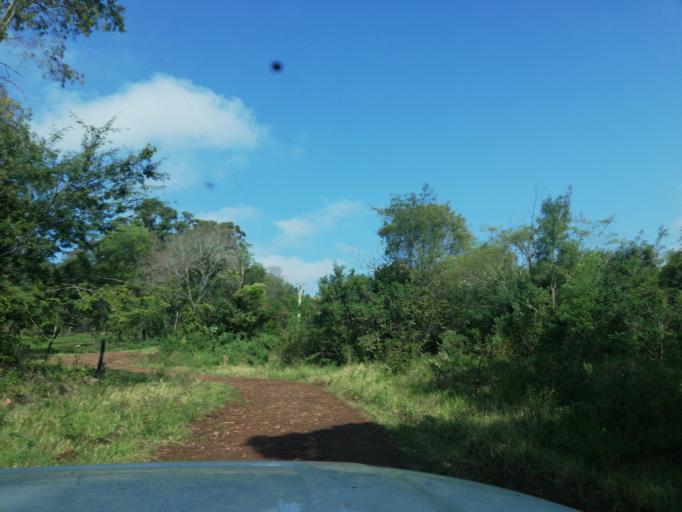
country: AR
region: Misiones
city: Cerro Azul
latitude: -27.6048
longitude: -55.5373
